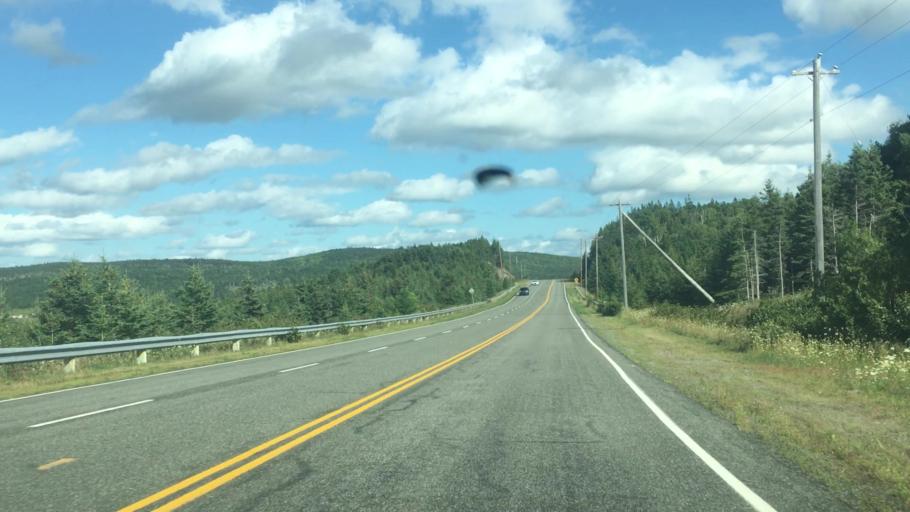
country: CA
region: Nova Scotia
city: Sydney
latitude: 45.8153
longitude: -60.6886
